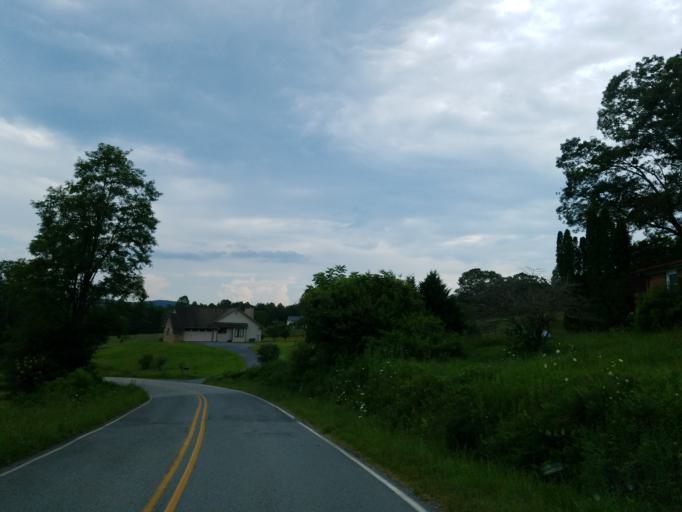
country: US
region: Georgia
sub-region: Fannin County
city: Blue Ridge
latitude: 34.8477
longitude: -84.2298
